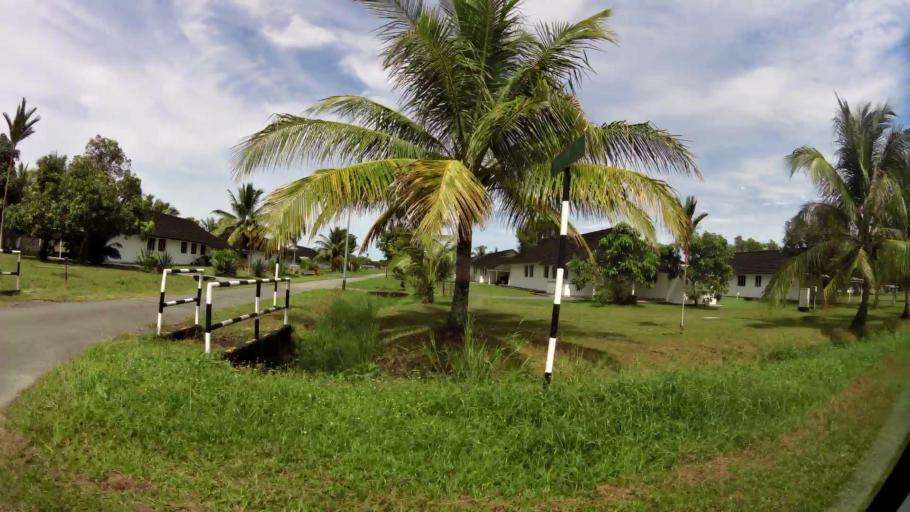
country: BN
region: Belait
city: Seria
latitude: 4.6114
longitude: 114.3229
